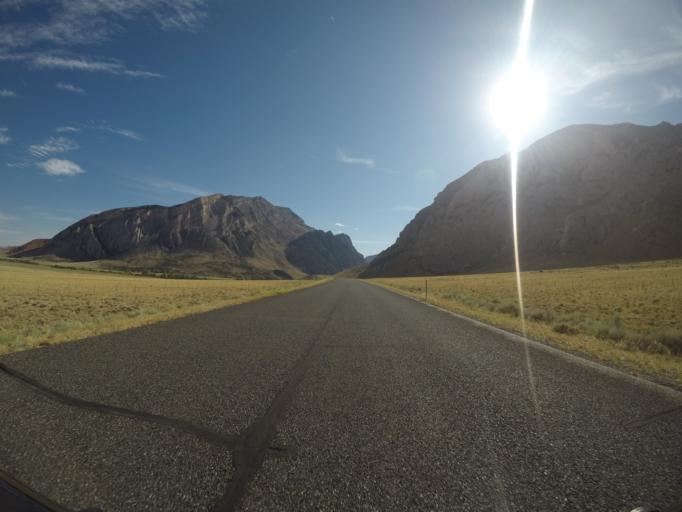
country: US
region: Montana
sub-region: Carbon County
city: Red Lodge
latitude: 44.8608
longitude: -109.2893
